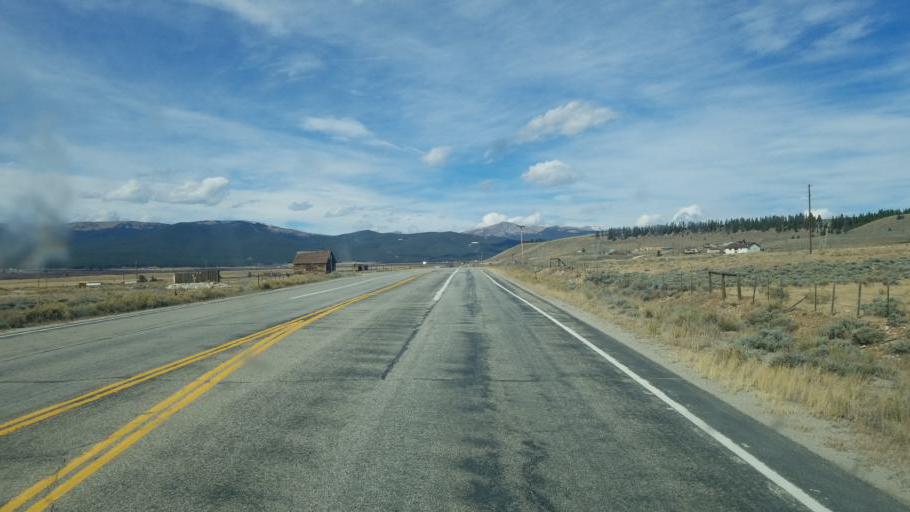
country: US
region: Colorado
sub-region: Lake County
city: Leadville
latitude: 39.1911
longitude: -106.3330
